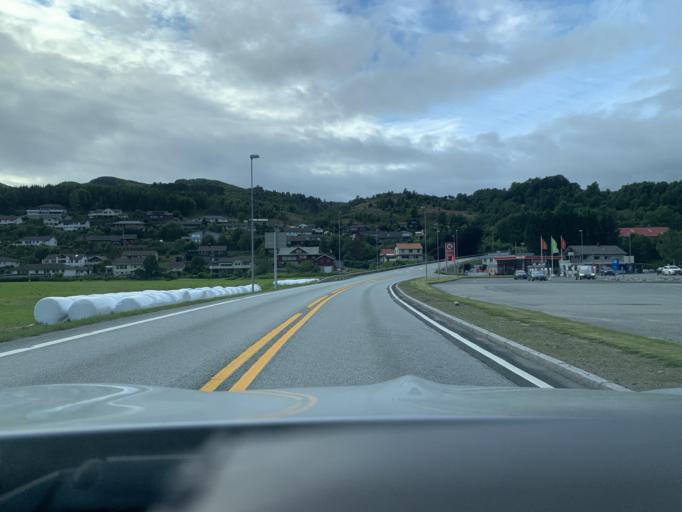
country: NO
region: Rogaland
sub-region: Bjerkreim
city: Vikesa
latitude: 58.6310
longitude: 6.0781
